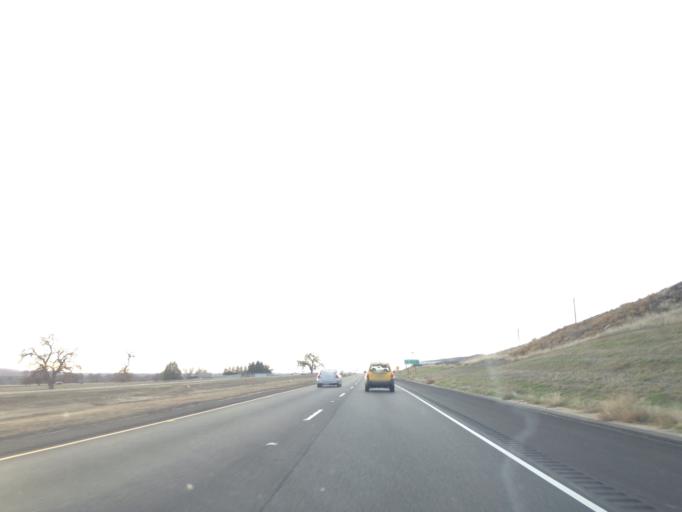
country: US
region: California
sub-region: San Luis Obispo County
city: Shandon
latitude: 35.6617
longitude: -120.4091
